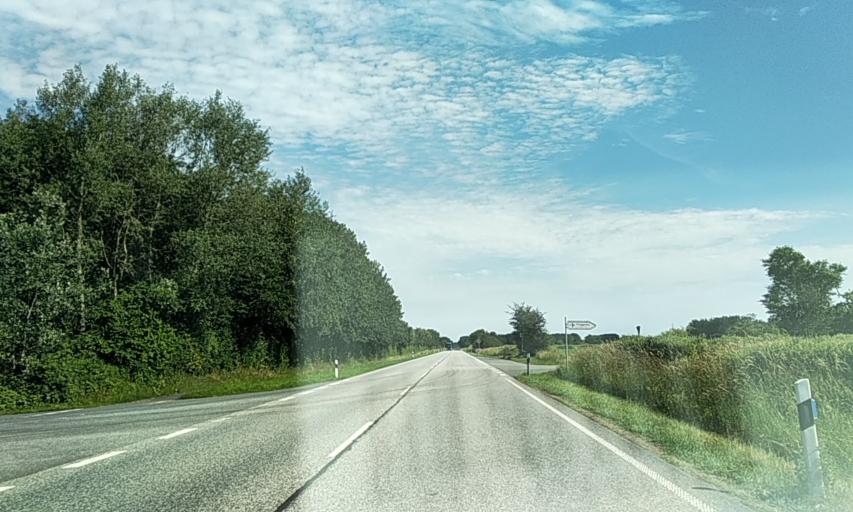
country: DE
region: Schleswig-Holstein
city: Kropp
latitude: 54.4277
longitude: 9.5316
